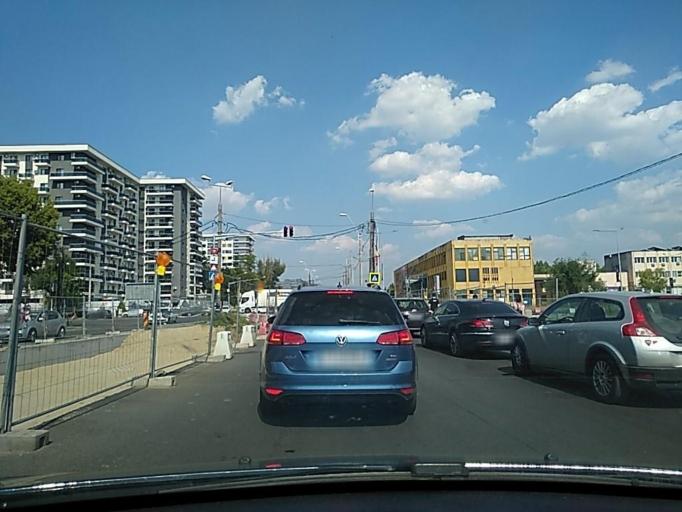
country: RO
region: Ilfov
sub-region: Comuna Chiajna
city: Rosu
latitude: 44.4139
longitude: 26.0341
